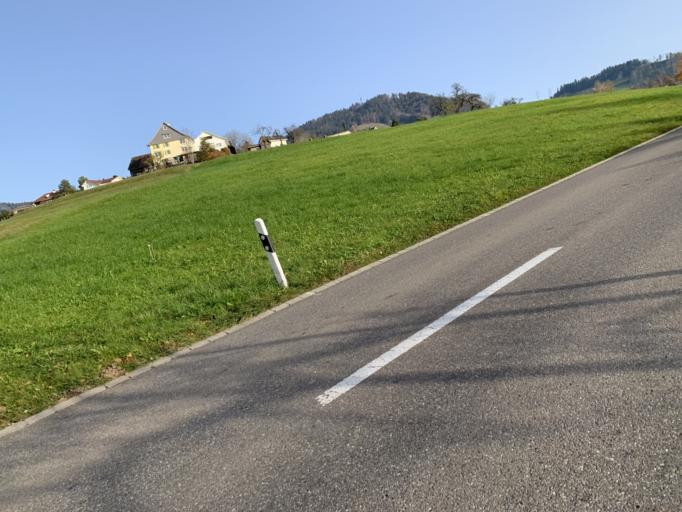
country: CH
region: Zurich
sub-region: Bezirk Hinwil
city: Hadlikon
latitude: 47.2987
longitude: 8.8576
